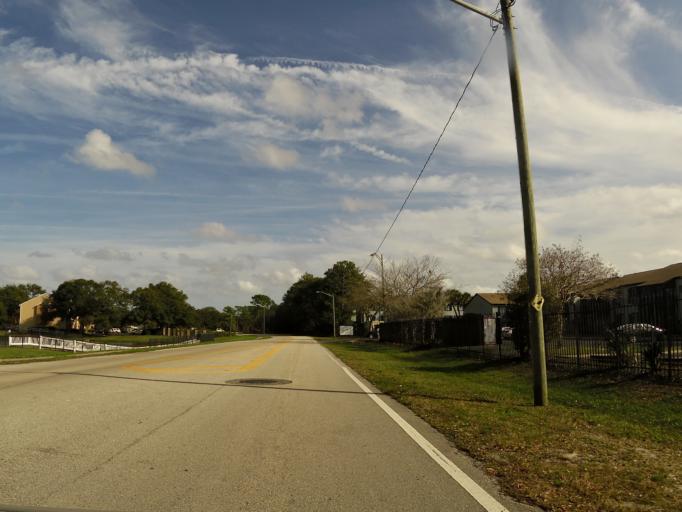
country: US
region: Florida
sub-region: Duval County
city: Jacksonville
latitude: 30.3307
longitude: -81.5454
